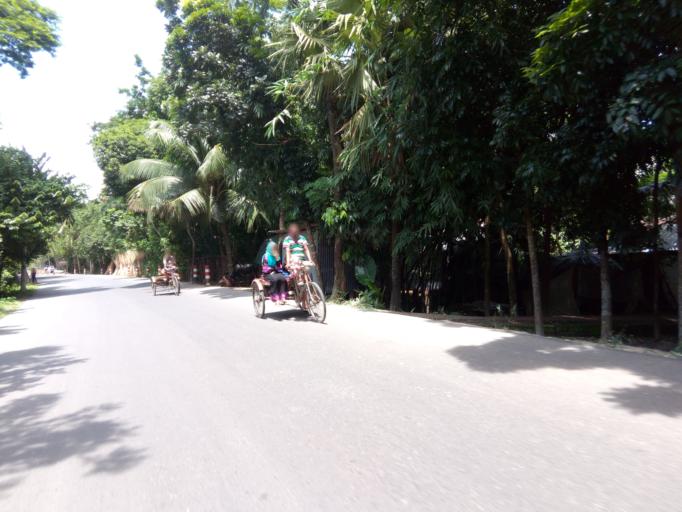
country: BD
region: Dhaka
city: Tungipara
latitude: 22.8988
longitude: 89.8886
